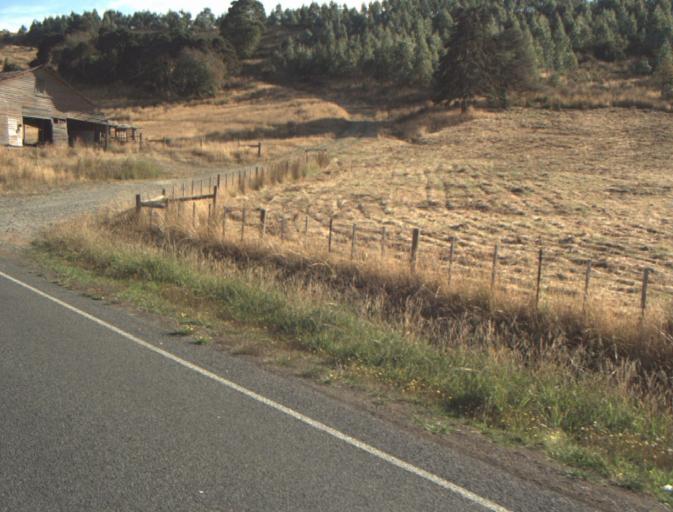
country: AU
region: Tasmania
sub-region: Launceston
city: Mayfield
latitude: -41.2377
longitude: 147.2154
